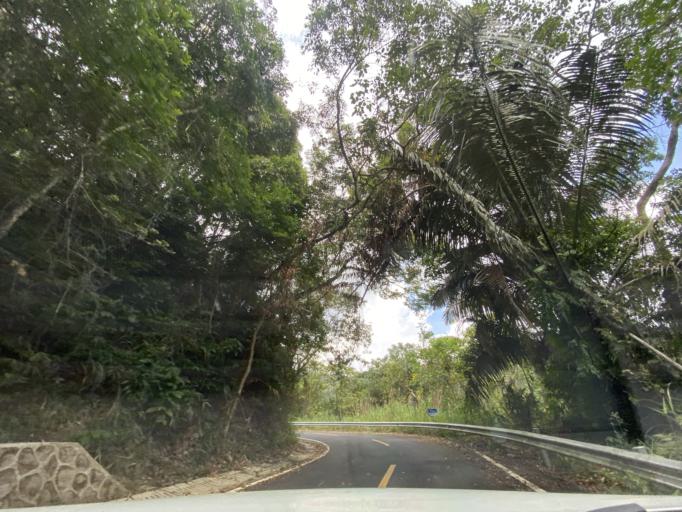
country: CN
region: Hainan
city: Benhao
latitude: 18.6882
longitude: 109.8782
